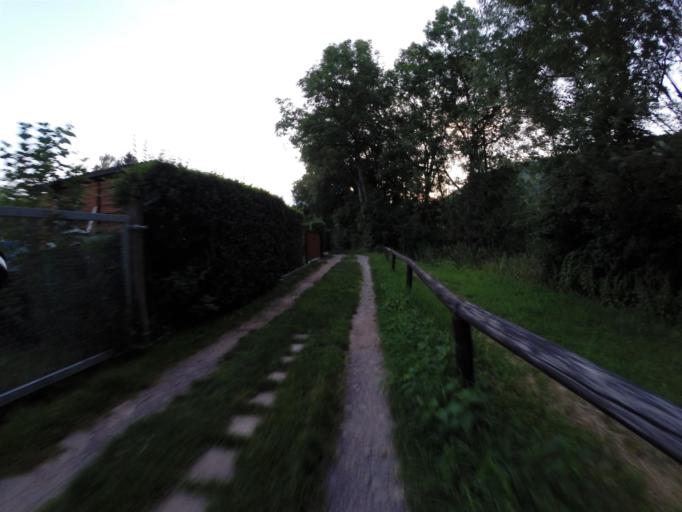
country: DE
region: Thuringia
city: Jena
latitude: 50.9331
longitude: 11.6305
